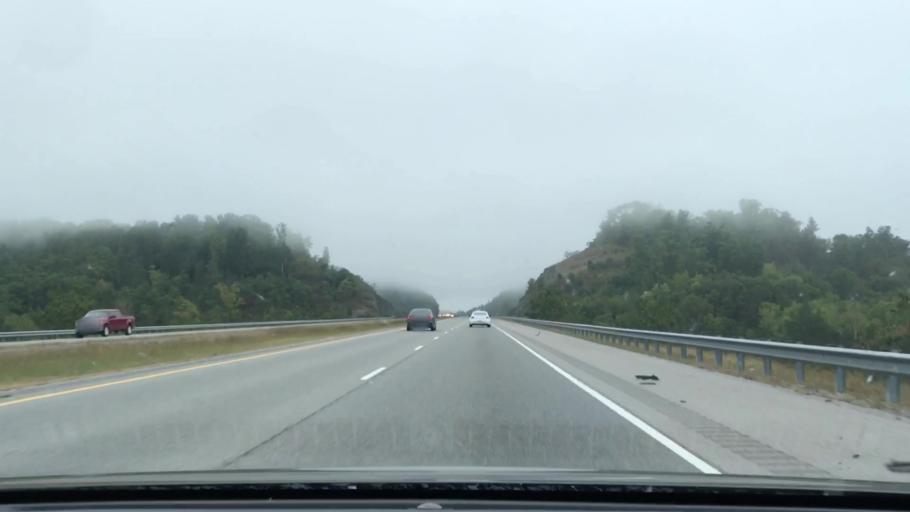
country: US
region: Tennessee
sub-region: Sumner County
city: Gallatin
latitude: 36.4590
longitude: -86.4677
